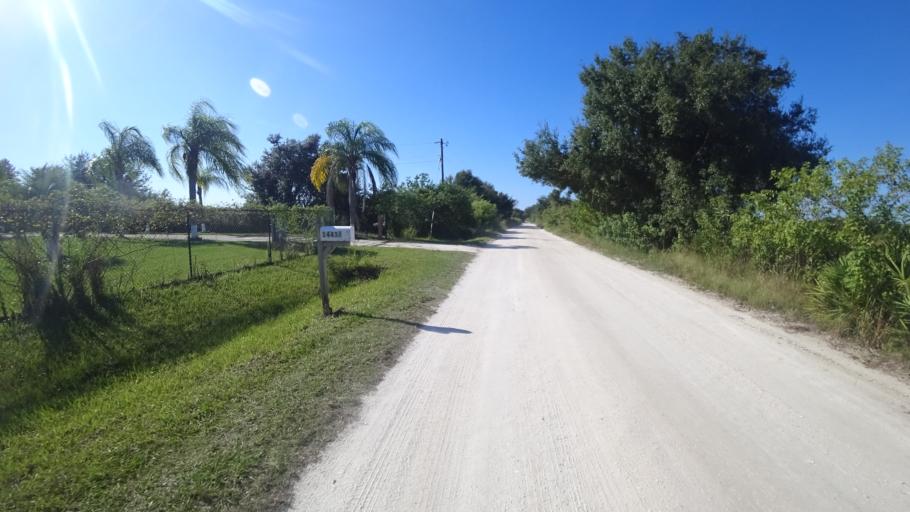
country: US
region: Florida
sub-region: Hillsborough County
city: Sun City Center
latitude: 27.6460
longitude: -82.3582
